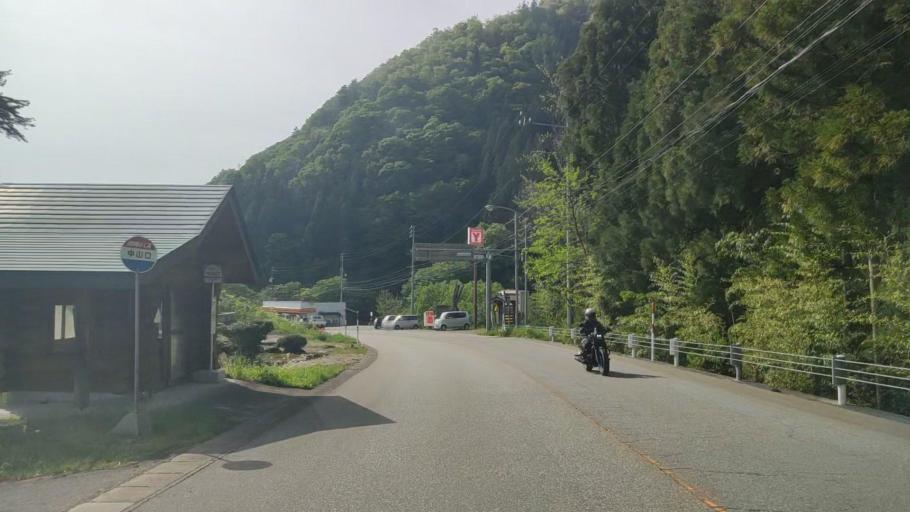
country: JP
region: Gifu
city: Takayama
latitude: 36.2955
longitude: 137.3701
